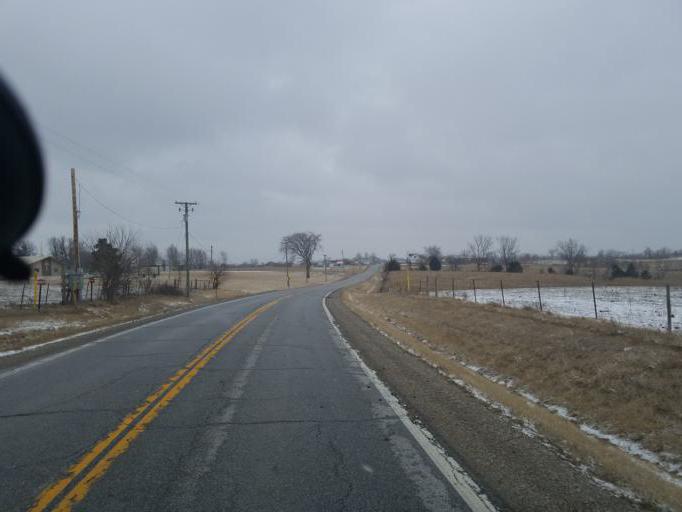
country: US
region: Missouri
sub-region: Putnam County
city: Unionville
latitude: 40.4996
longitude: -93.0095
